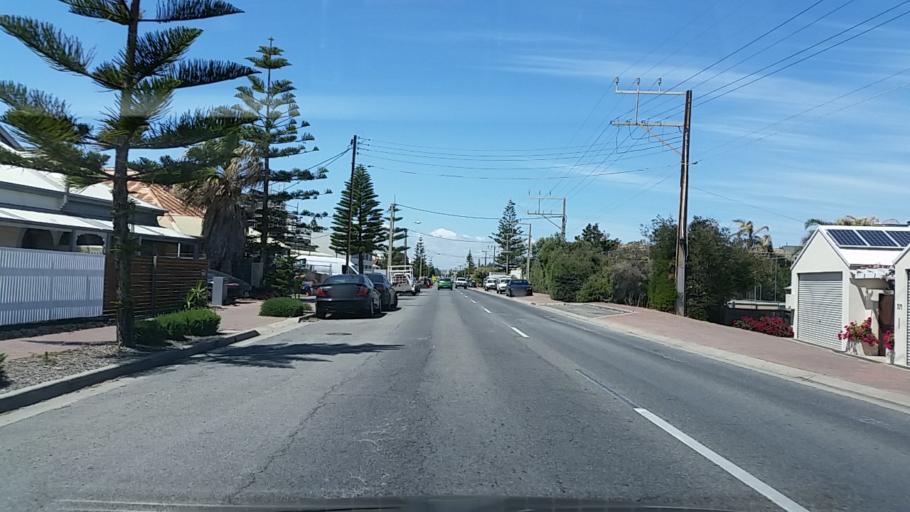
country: AU
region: South Australia
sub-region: Charles Sturt
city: Henley Beach
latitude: -34.9115
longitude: 138.4922
